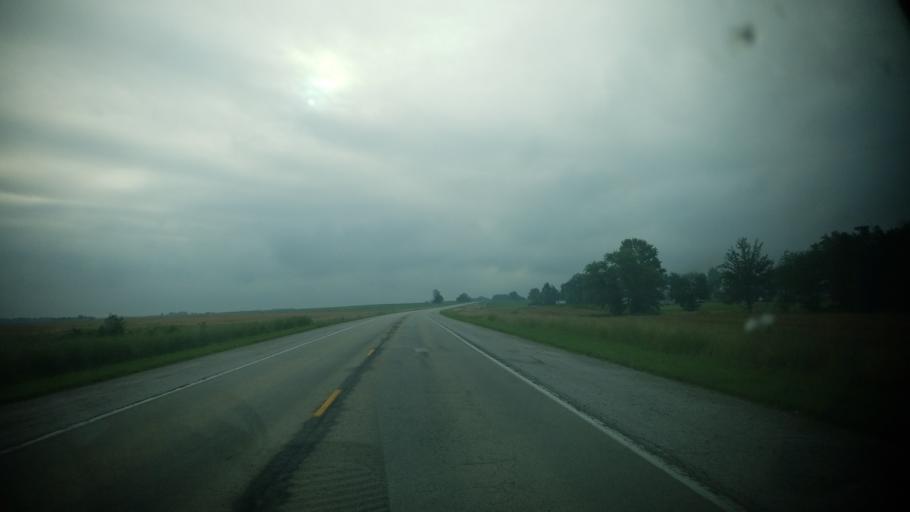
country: US
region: Illinois
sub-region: Clay County
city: Flora
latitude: 38.6767
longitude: -88.4207
